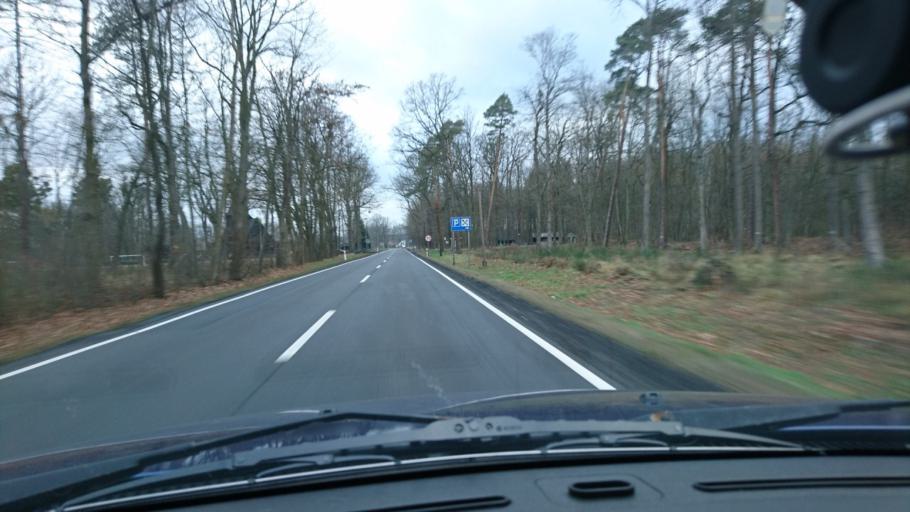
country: PL
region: Opole Voivodeship
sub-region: Powiat oleski
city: Olesno
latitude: 50.9091
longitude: 18.3606
